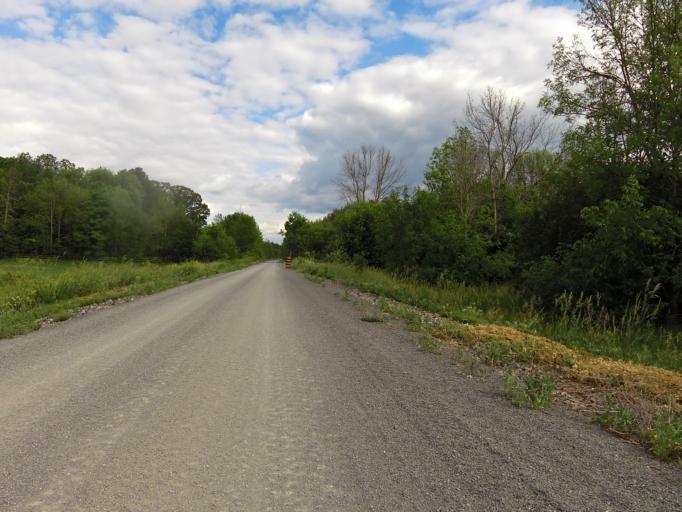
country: CA
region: Ontario
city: Arnprior
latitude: 45.2863
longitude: -76.2502
